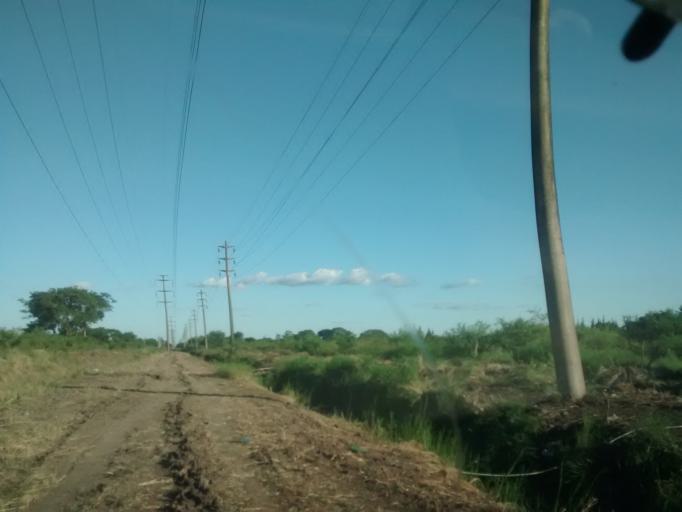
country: AR
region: Chaco
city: Fontana
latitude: -27.4066
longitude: -58.9938
